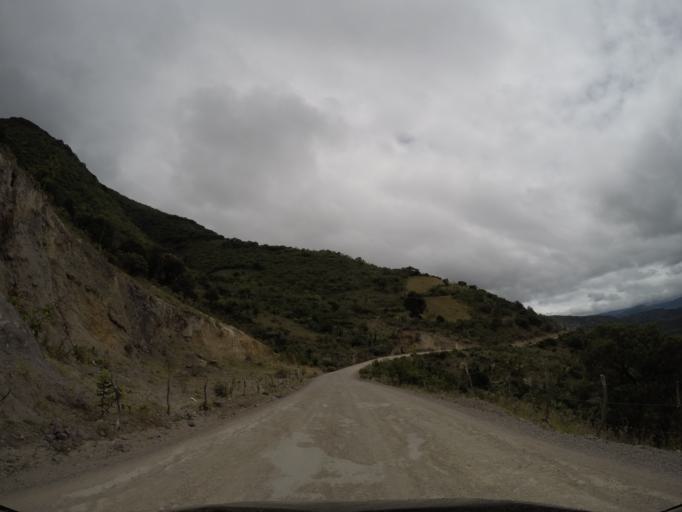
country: MX
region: Oaxaca
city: San Lorenzo Albarradas
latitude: 16.8910
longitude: -96.2644
